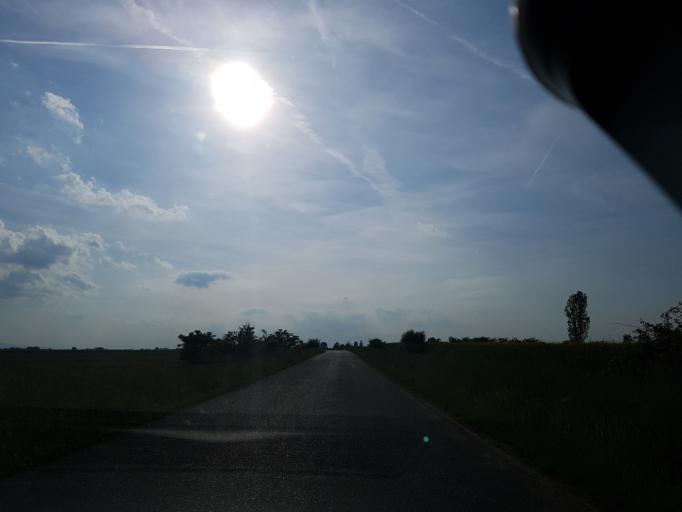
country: PL
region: Lower Silesian Voivodeship
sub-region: Powiat strzelinski
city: Wiazow
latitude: 50.8400
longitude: 17.2081
